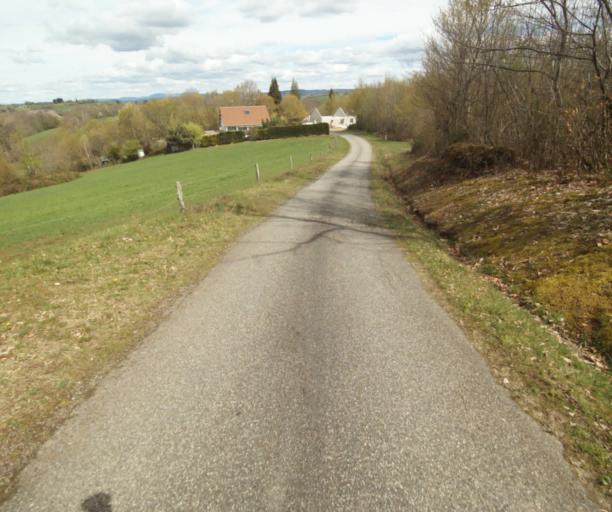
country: FR
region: Limousin
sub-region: Departement de la Correze
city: Sainte-Fortunade
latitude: 45.2060
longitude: 1.8370
